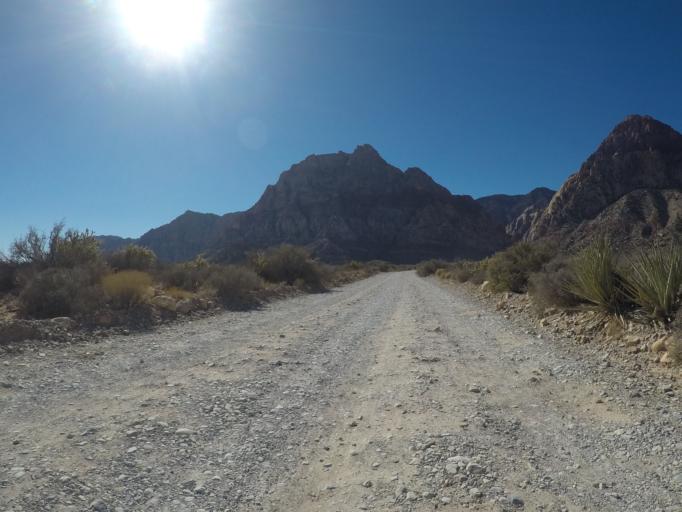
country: US
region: Nevada
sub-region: Clark County
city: Summerlin South
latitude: 36.1122
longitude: -115.4643
